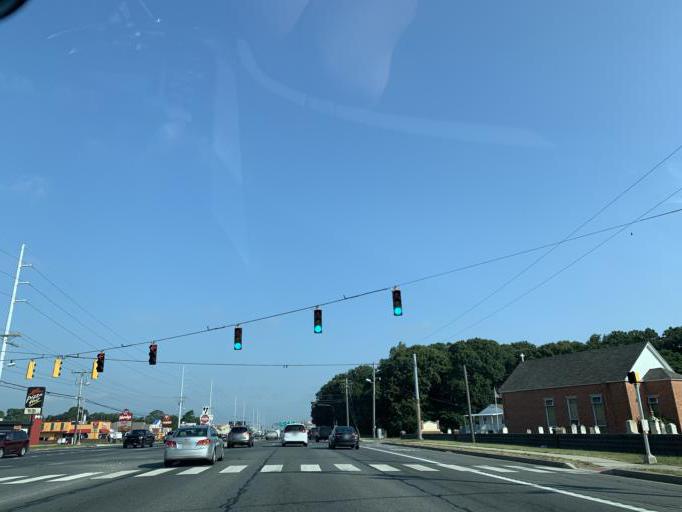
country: US
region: Delaware
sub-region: Sussex County
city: Lewes
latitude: 38.7279
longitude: -75.1288
